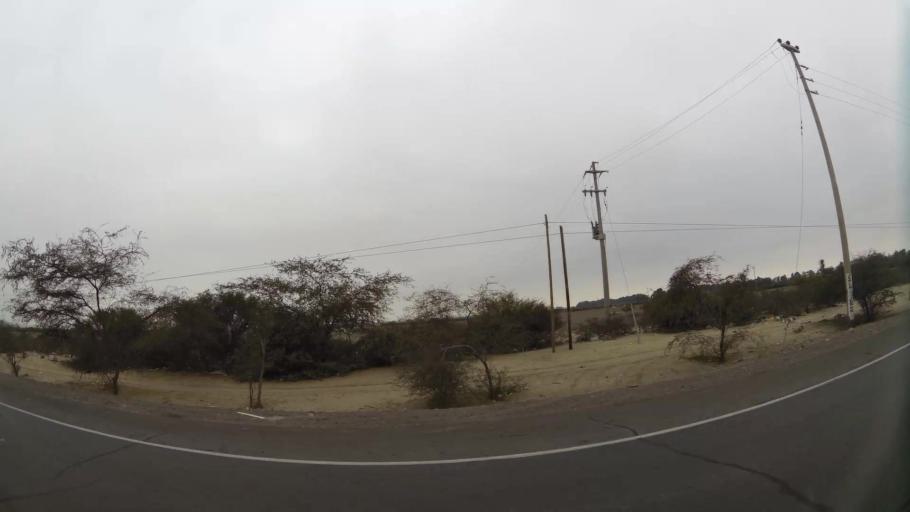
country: PE
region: Ica
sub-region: Provincia de Pisco
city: Villa Tupac Amaru
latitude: -13.8135
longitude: -76.1487
